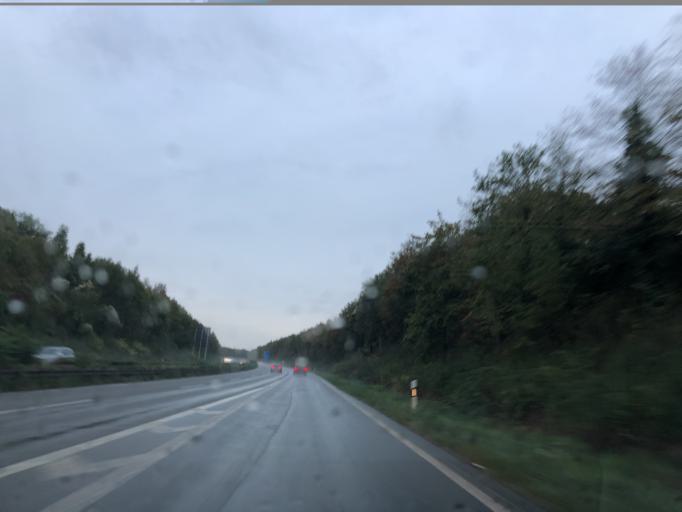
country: DE
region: North Rhine-Westphalia
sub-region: Regierungsbezirk Dusseldorf
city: Hochfeld
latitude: 51.3684
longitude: 6.7706
